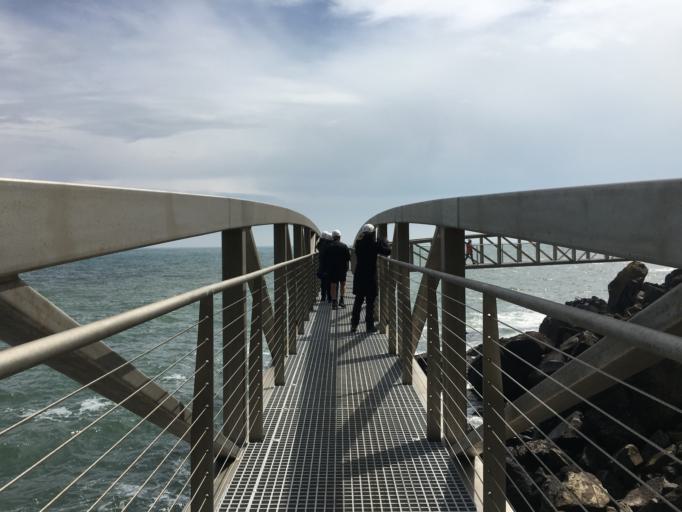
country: GB
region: Northern Ireland
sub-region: Carrickfergus District
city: Whitehead
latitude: 54.8075
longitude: -5.6915
